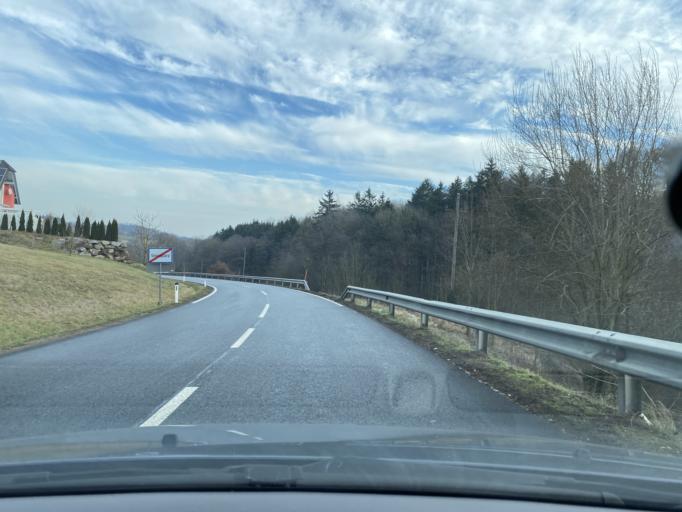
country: AT
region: Lower Austria
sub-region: Politischer Bezirk Melk
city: Loosdorf
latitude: 48.1687
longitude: 15.3551
